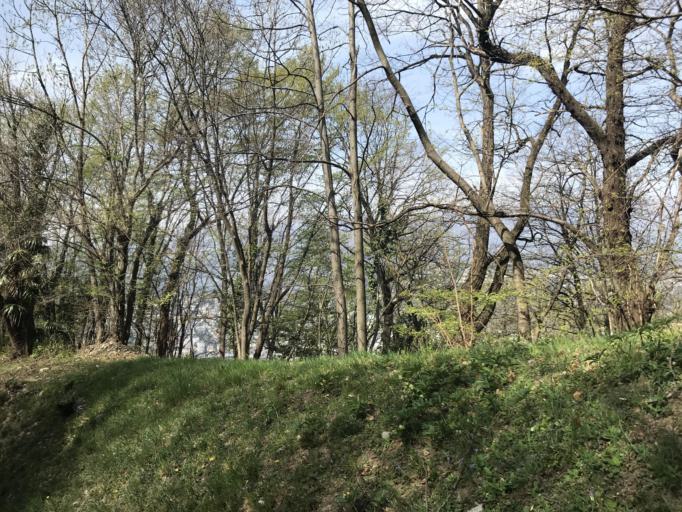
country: CH
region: Ticino
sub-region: Lugano District
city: Viganello
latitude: 46.0099
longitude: 8.9775
